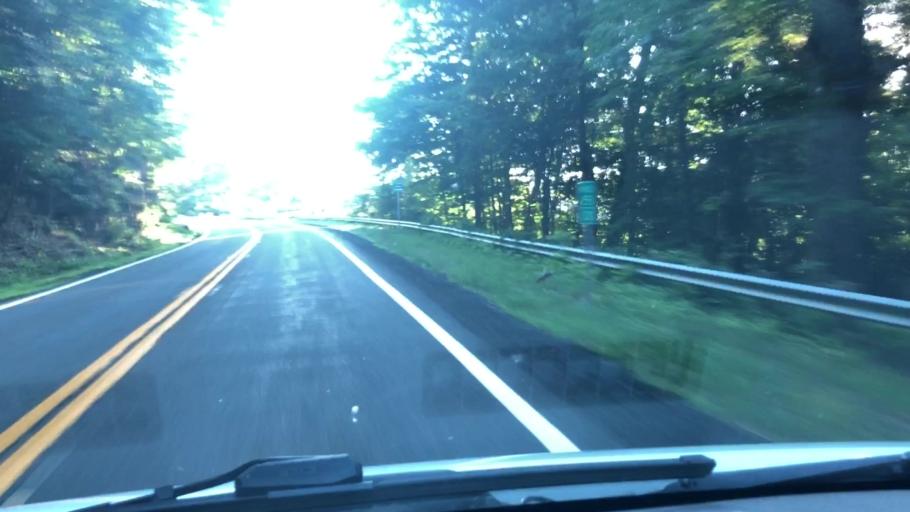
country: US
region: Massachusetts
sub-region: Hampshire County
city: Westhampton
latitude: 42.2956
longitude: -72.8694
